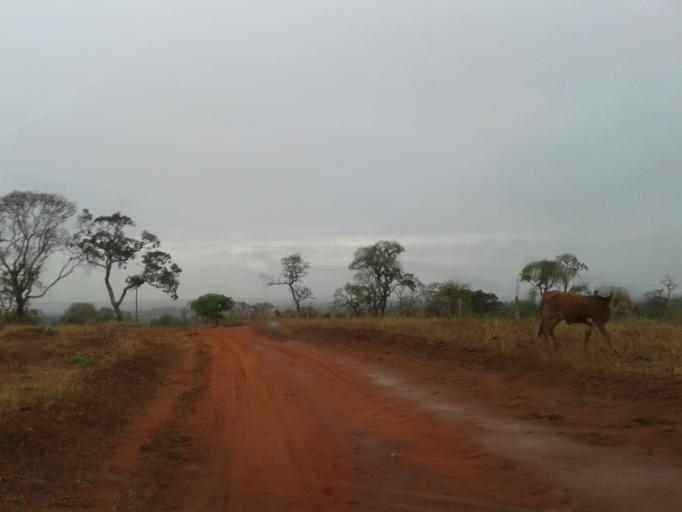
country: BR
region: Minas Gerais
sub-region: Campina Verde
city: Campina Verde
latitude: -19.3079
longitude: -49.5058
